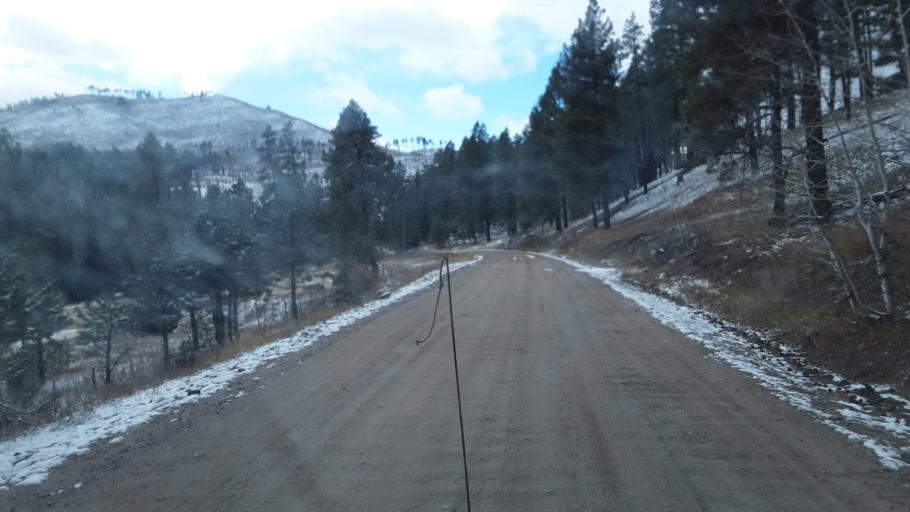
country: US
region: Colorado
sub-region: La Plata County
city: Bayfield
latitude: 37.4148
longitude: -107.5150
